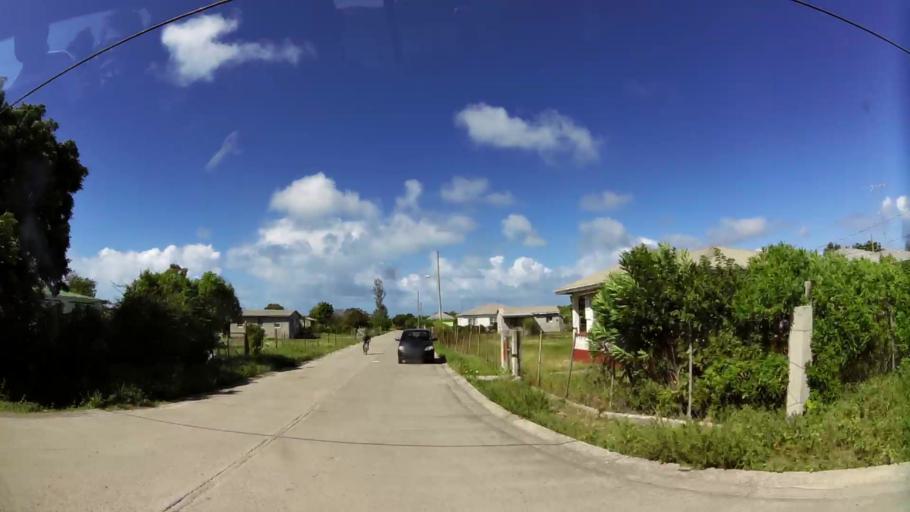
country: AG
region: Barbuda
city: Codrington
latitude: 17.6449
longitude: -61.8229
